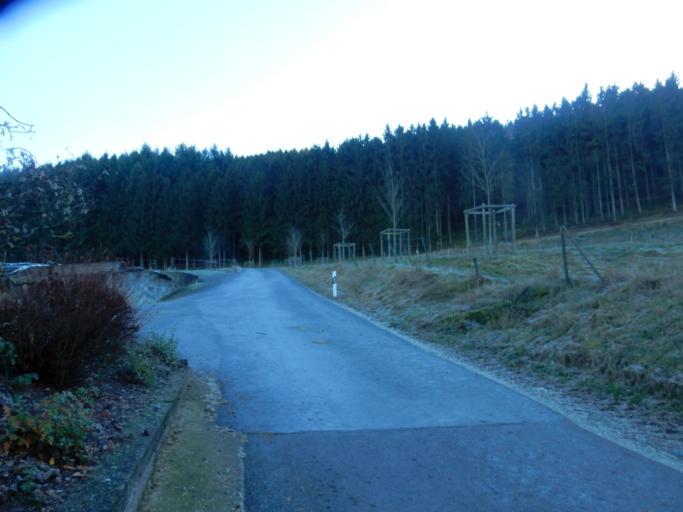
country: LU
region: Diekirch
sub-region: Canton de Diekirch
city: Bourscheid
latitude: 49.9198
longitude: 6.0652
